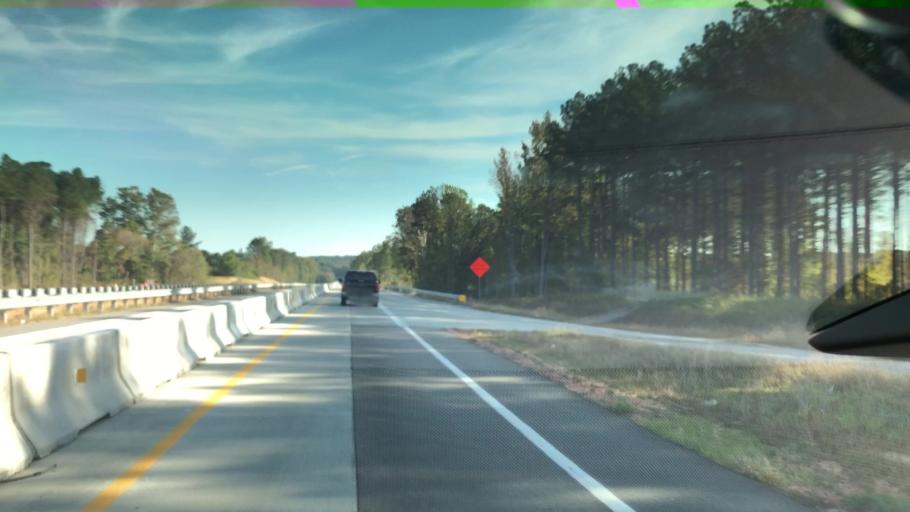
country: US
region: North Carolina
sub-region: Vance County
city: Henderson
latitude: 36.3626
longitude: -78.3730
